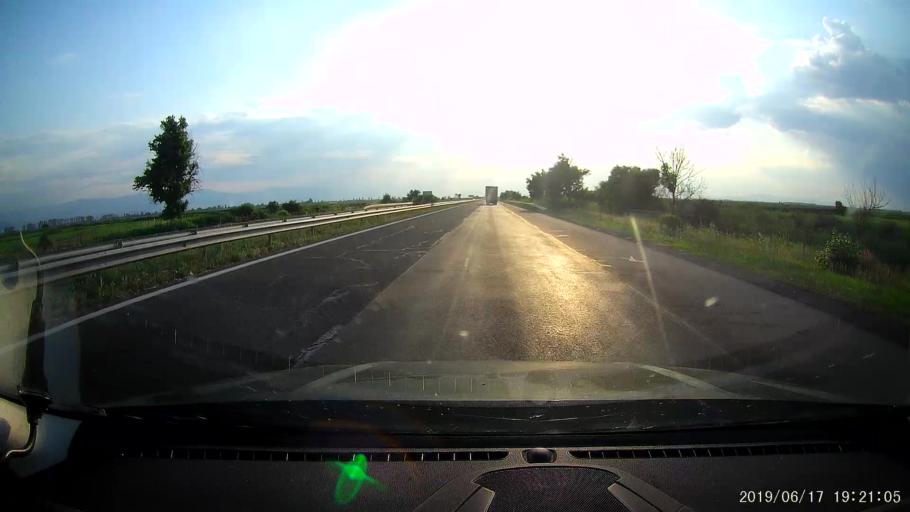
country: BG
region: Plovdiv
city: Stamboliyski
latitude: 42.2074
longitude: 24.4741
